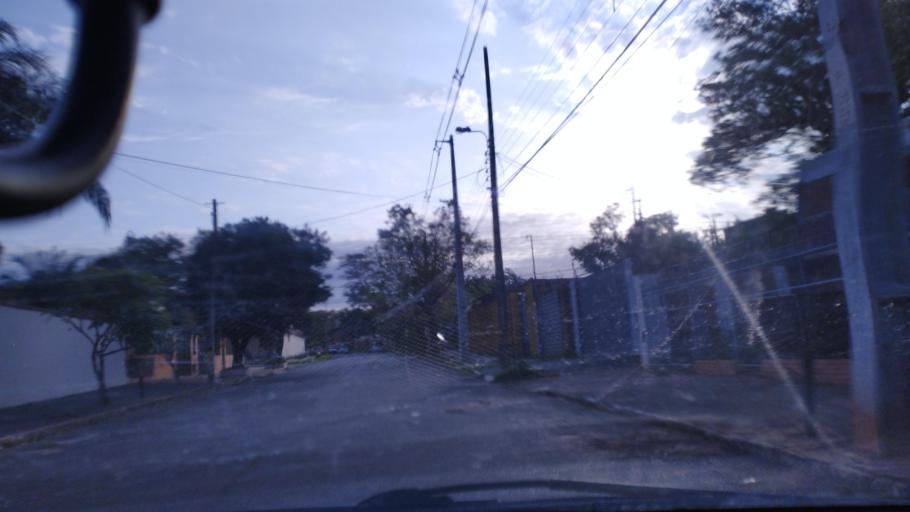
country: PY
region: Central
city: Fernando de la Mora
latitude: -25.3106
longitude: -57.5349
